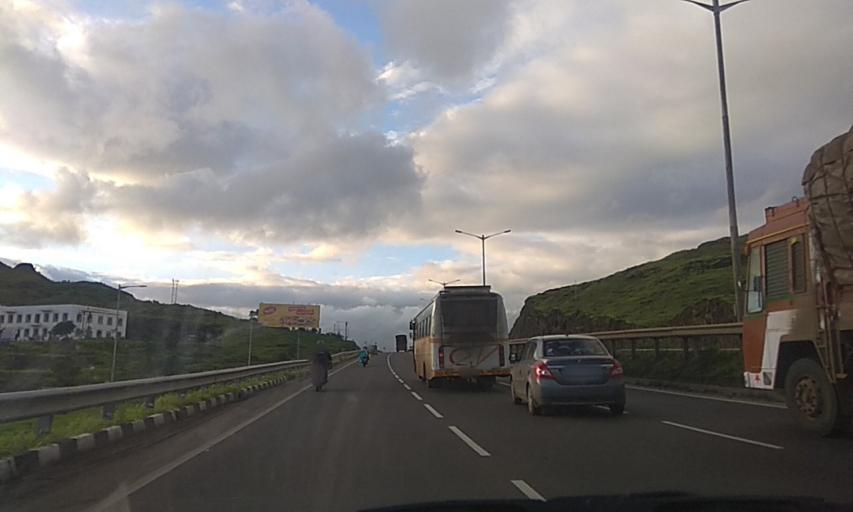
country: IN
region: Maharashtra
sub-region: Satara Division
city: Satara
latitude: 17.7547
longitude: 73.9940
